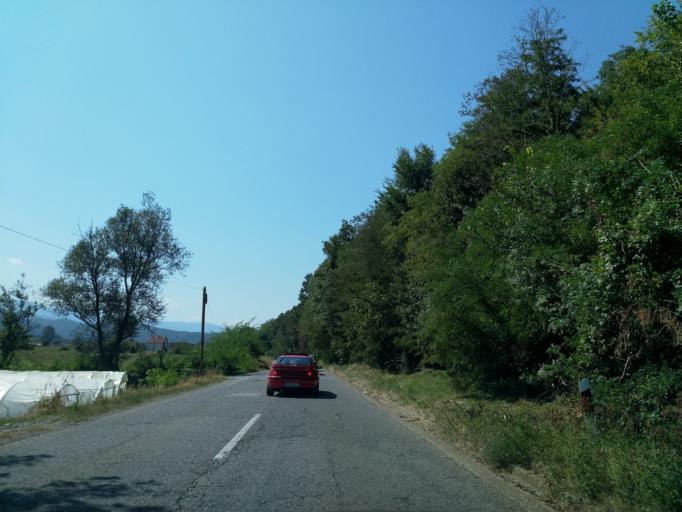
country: RS
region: Central Serbia
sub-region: Rasinski Okrug
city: Trstenik
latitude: 43.6319
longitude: 21.0112
